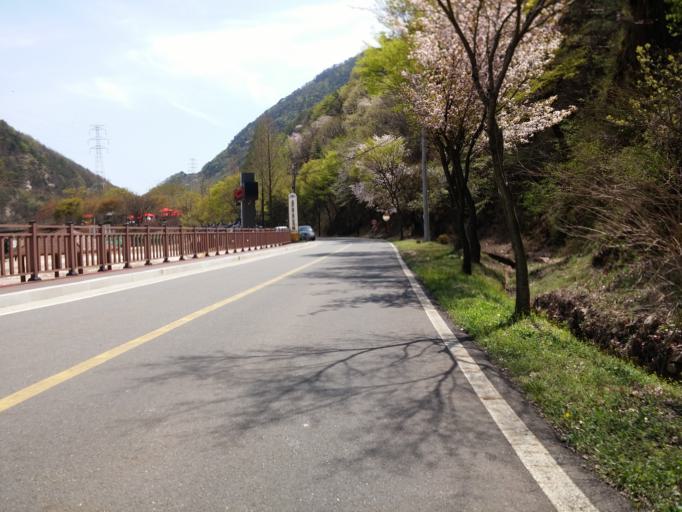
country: KR
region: Chungcheongbuk-do
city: Okcheon
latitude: 36.2444
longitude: 127.5535
